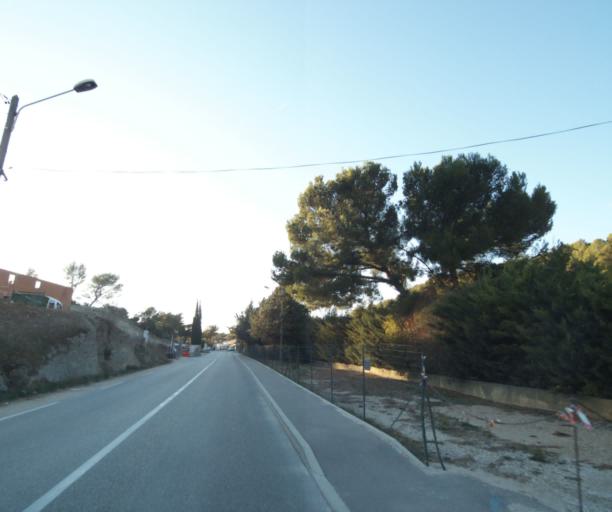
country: FR
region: Provence-Alpes-Cote d'Azur
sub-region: Departement des Bouches-du-Rhone
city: Roquefort-la-Bedoule
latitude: 43.2478
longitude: 5.5781
